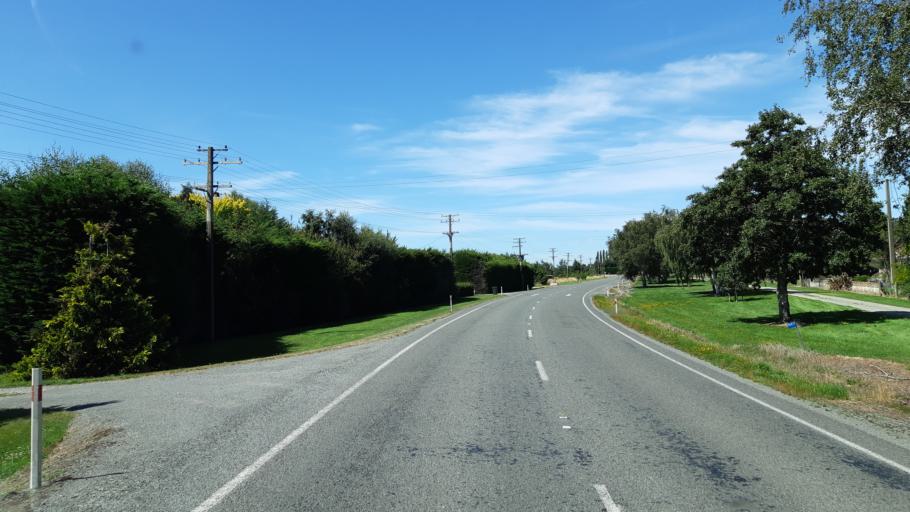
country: NZ
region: Southland
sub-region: Gore District
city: Gore
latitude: -45.9925
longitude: 168.8115
